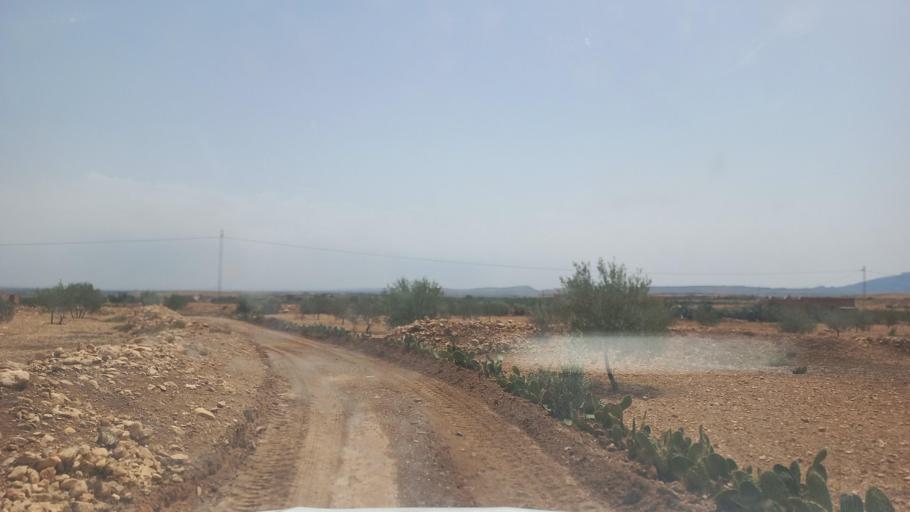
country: TN
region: Al Qasrayn
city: Kasserine
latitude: 35.2978
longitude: 8.9385
